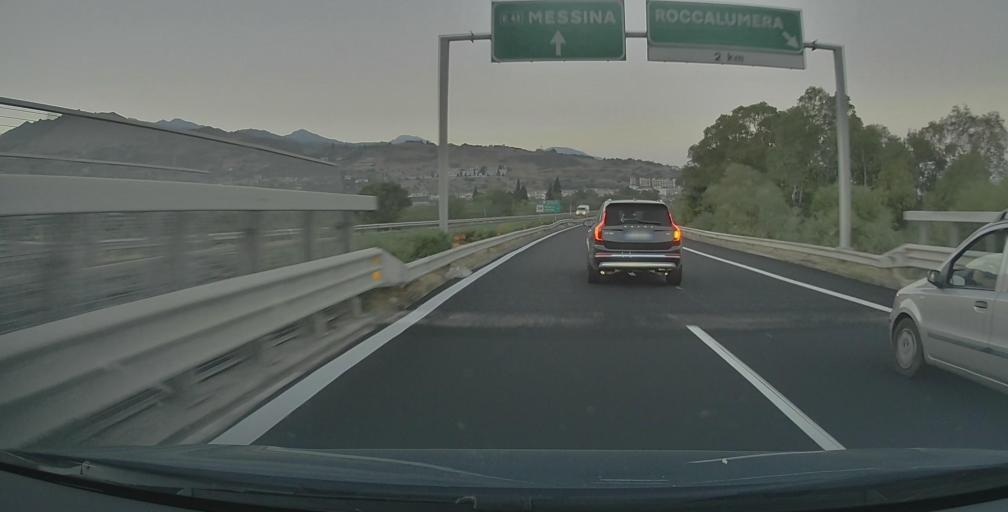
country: IT
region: Sicily
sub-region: Messina
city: Furci Siculo
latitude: 37.9555
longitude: 15.3707
